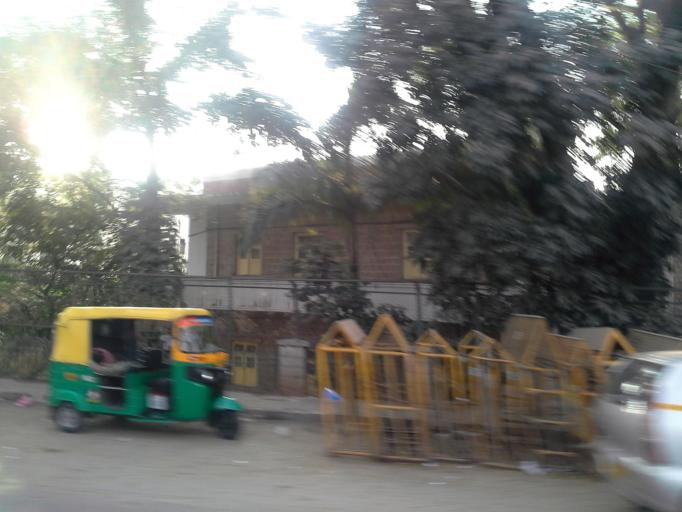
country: IN
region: Karnataka
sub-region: Bangalore Urban
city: Bangalore
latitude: 12.9825
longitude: 77.5766
